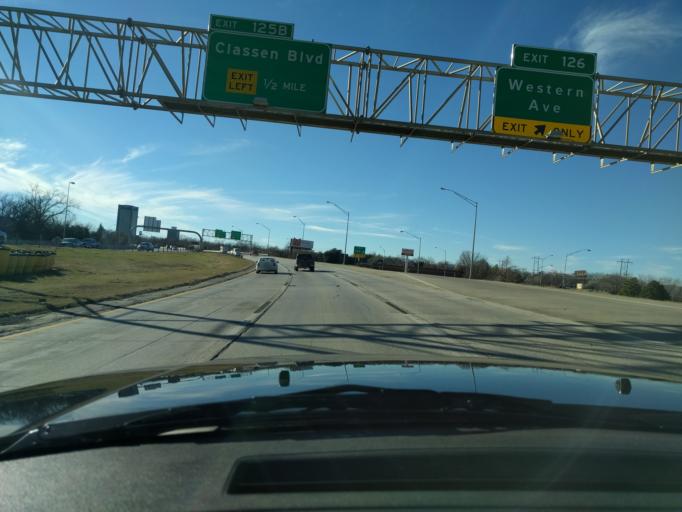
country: US
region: Oklahoma
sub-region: Oklahoma County
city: Nichols Hills
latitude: 35.5283
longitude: -97.5248
